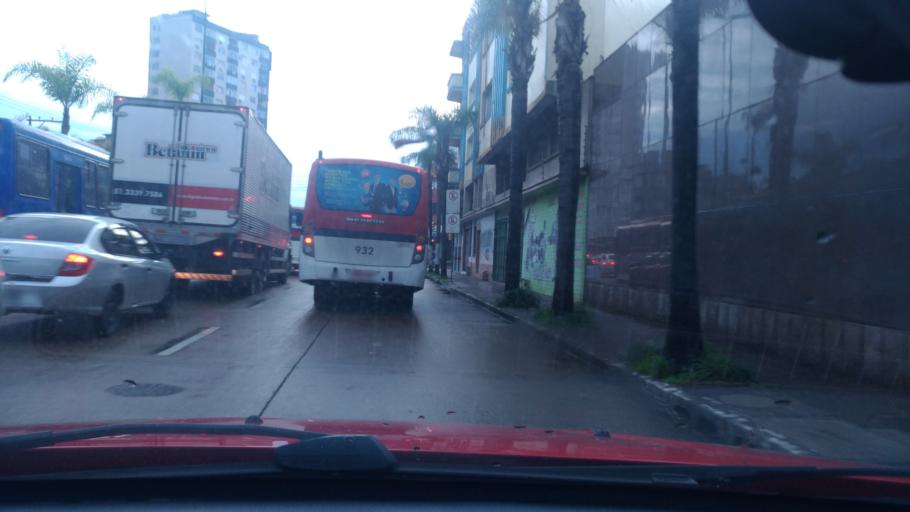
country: BR
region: Rio Grande do Sul
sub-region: Porto Alegre
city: Porto Alegre
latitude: -30.0153
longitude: -51.2058
